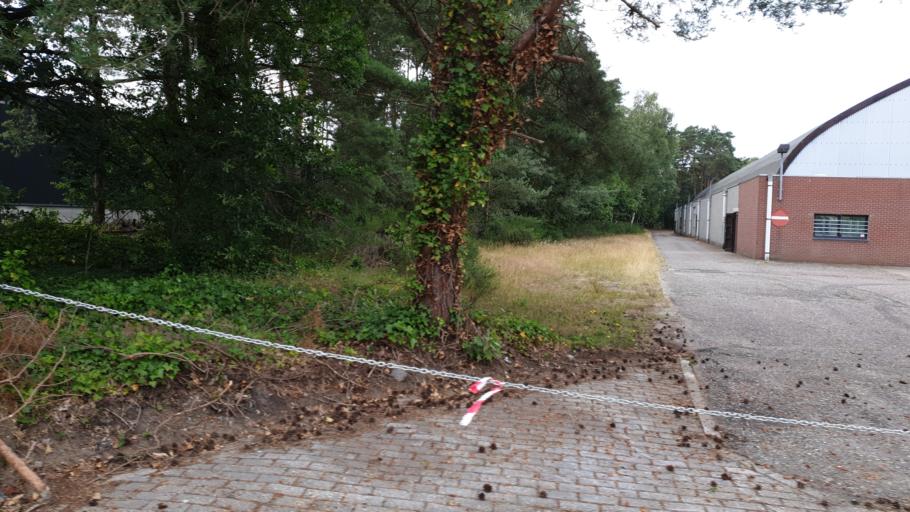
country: BE
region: Flanders
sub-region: Provincie Antwerpen
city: Meerhout
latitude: 51.1646
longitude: 5.0425
